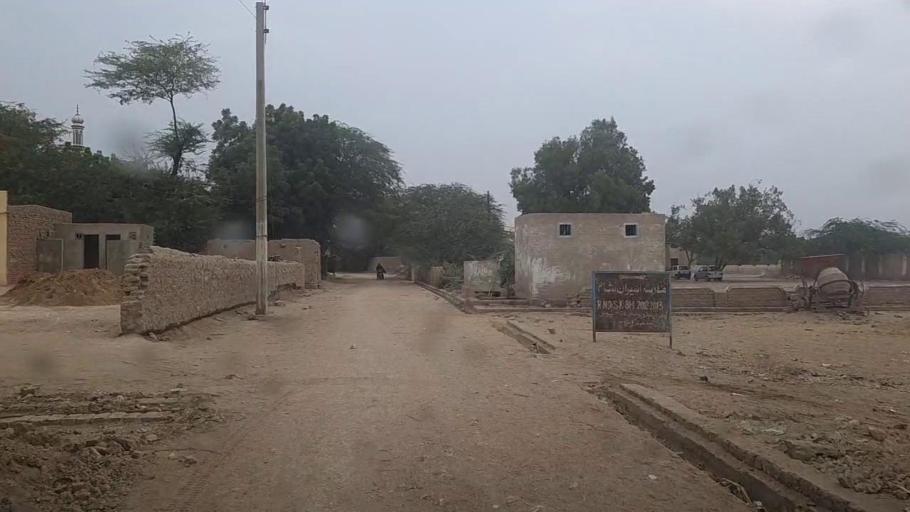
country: PK
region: Sindh
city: Gambat
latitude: 27.3570
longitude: 68.5977
